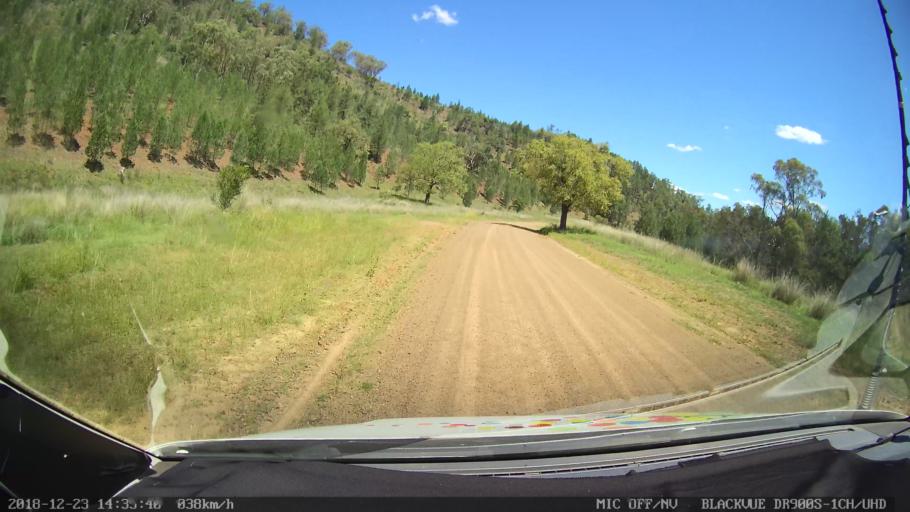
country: AU
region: New South Wales
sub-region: Tamworth Municipality
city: Manilla
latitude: -30.6118
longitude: 150.9082
